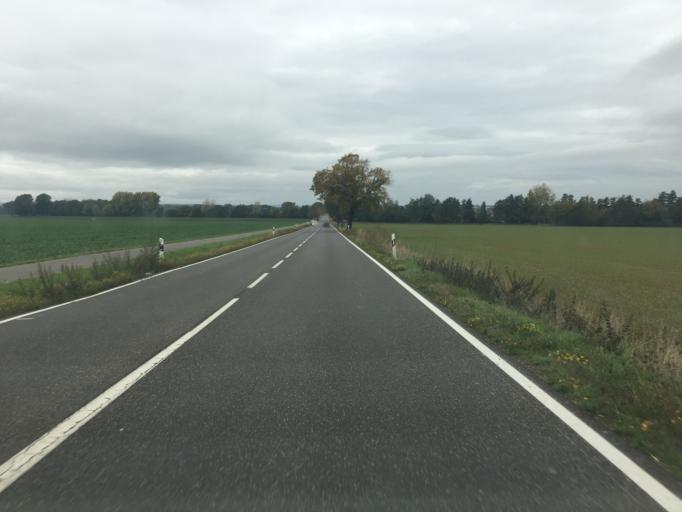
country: DE
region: North Rhine-Westphalia
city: Zulpich
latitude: 50.6776
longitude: 6.6907
